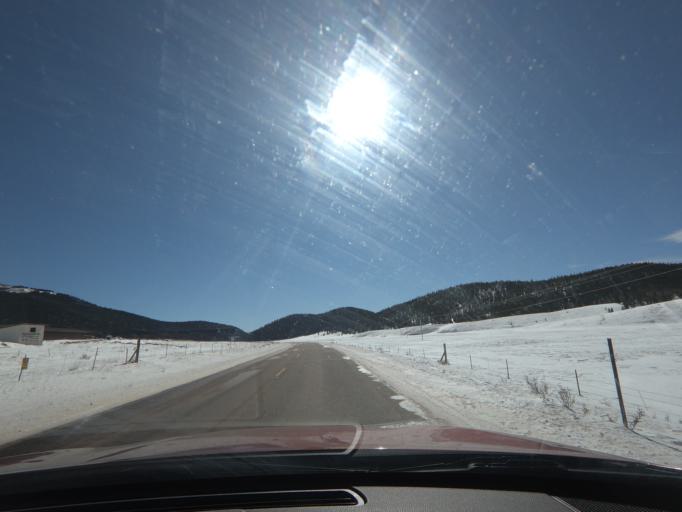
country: US
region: Colorado
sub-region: Teller County
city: Cripple Creek
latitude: 38.7652
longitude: -105.1166
